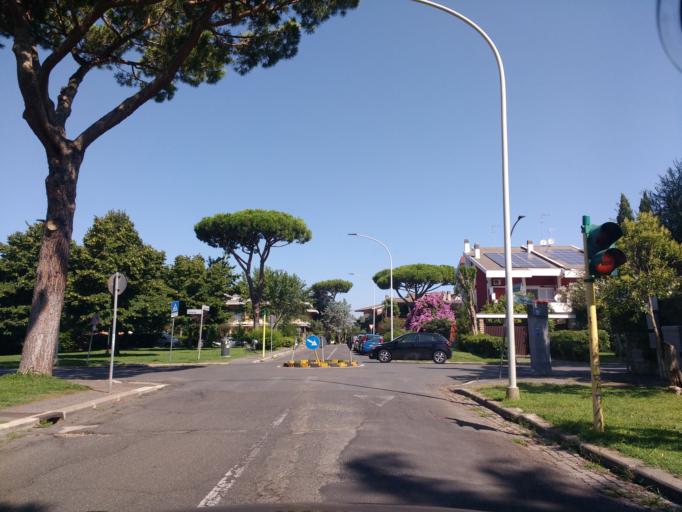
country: IT
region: Latium
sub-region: Citta metropolitana di Roma Capitale
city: Acilia-Castel Fusano-Ostia Antica
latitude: 41.7686
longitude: 12.3665
